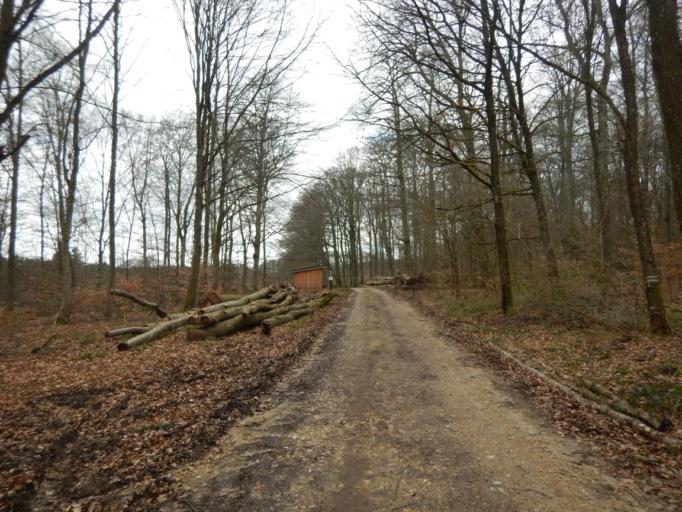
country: LU
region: Luxembourg
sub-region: Canton de Mersch
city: Tuntange
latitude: 49.7286
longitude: 6.0365
